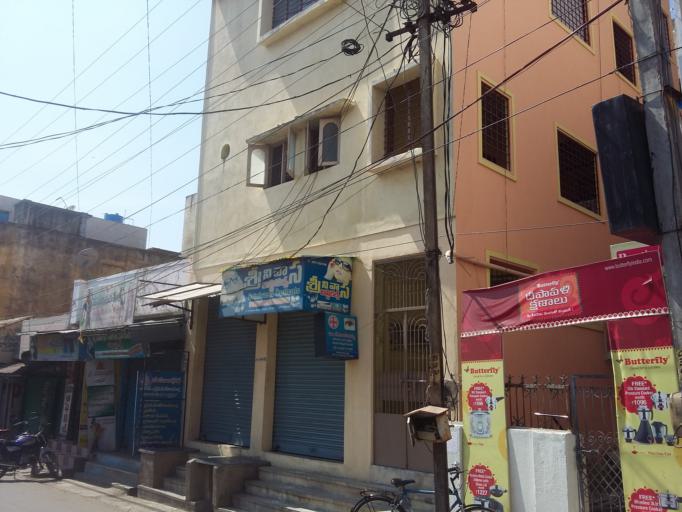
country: IN
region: Andhra Pradesh
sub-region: Chittoor
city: Tirupati
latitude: 13.6342
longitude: 79.4157
